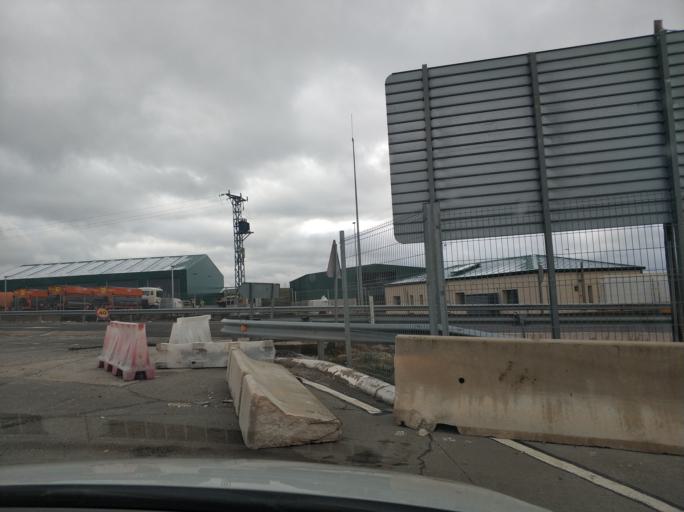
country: ES
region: Castille and Leon
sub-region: Provincia de Segovia
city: Cerezo de Abajo
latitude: 41.1900
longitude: -3.5834
